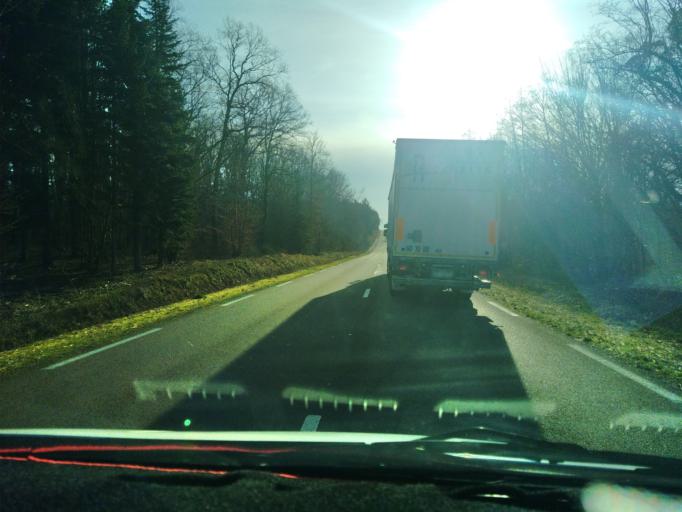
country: FR
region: Franche-Comte
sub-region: Departement de la Haute-Saone
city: Gray
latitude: 47.4068
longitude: 5.6362
